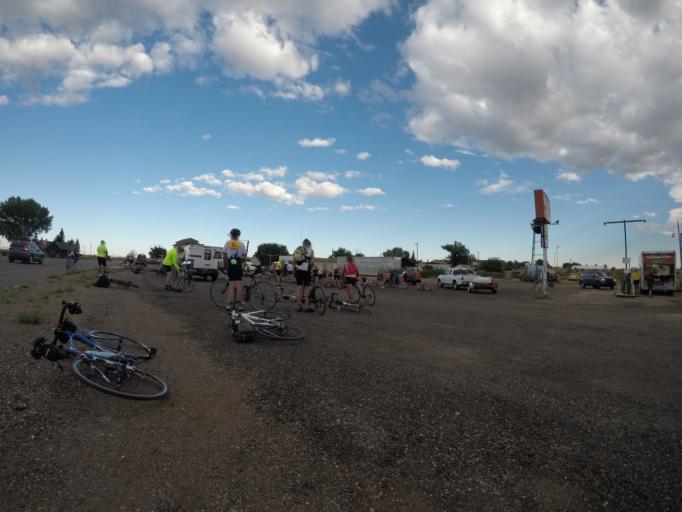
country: US
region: Wyoming
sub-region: Carbon County
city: Saratoga
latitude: 41.8957
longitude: -106.1983
